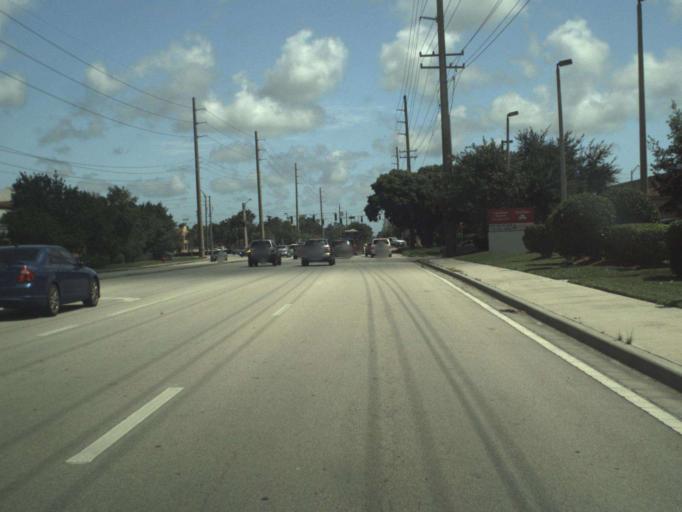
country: US
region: Florida
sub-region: Indian River County
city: West Vero Corridor
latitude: 27.6372
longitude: -80.4466
